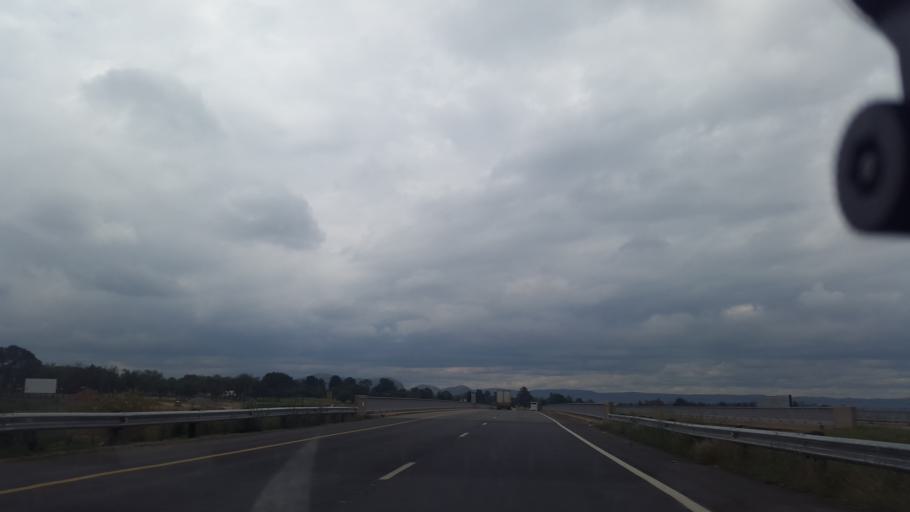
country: ZA
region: Gauteng
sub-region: West Rand District Municipality
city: Muldersdriseloop
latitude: -26.0210
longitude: 27.8606
